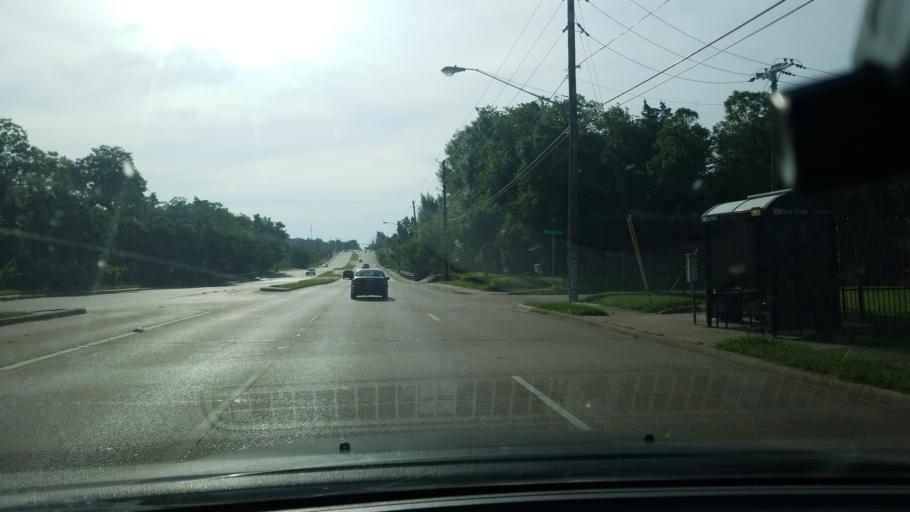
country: US
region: Texas
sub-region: Dallas County
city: Balch Springs
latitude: 32.7486
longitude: -96.6632
